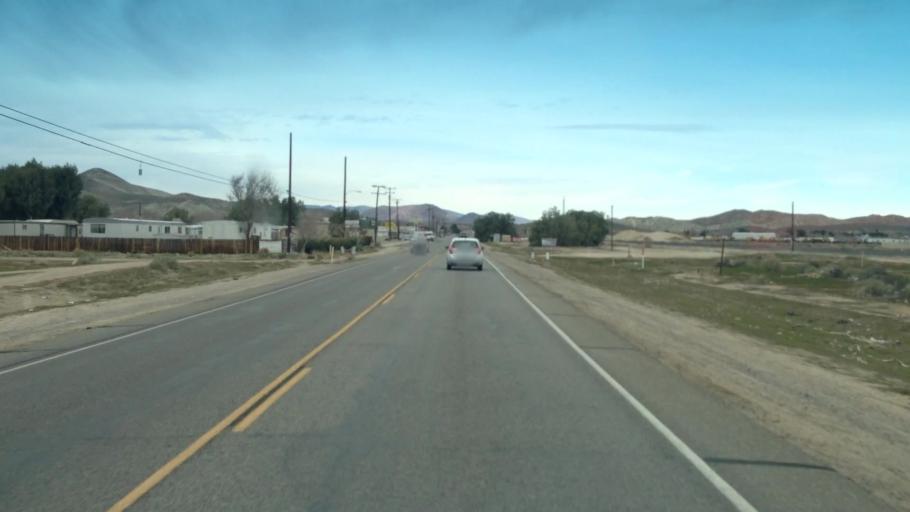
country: US
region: California
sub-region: Kern County
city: Rosamond
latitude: 34.8544
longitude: -118.1619
